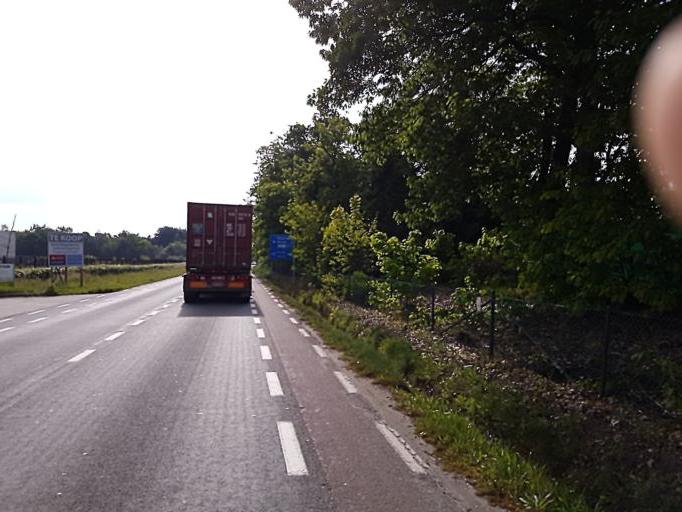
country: BE
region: Flanders
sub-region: Provincie Limburg
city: Overpelt
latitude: 51.2330
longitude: 5.4034
